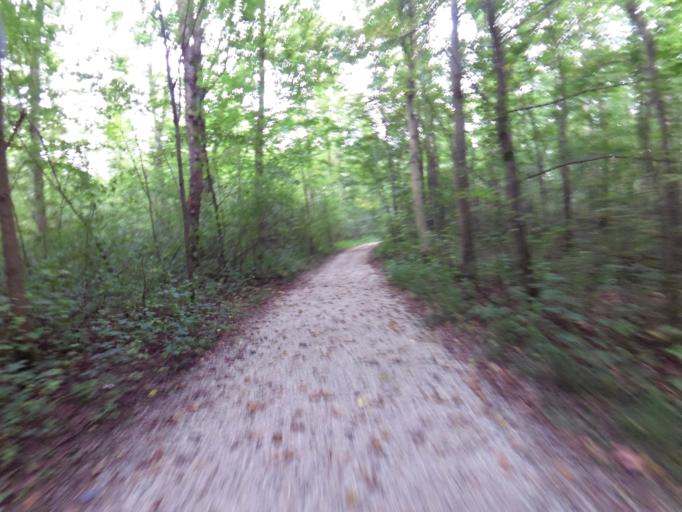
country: DE
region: Bavaria
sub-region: Lower Bavaria
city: Tiefenbach
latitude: 48.5243
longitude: 12.1165
